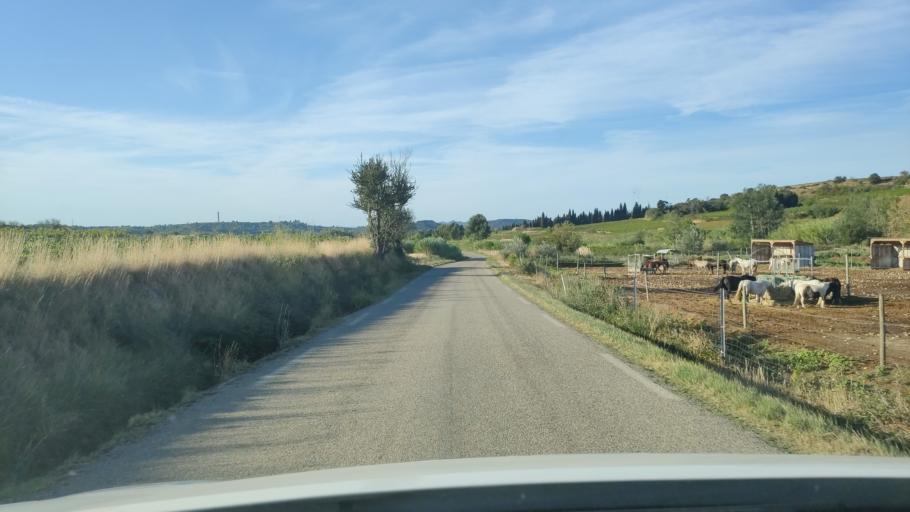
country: FR
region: Languedoc-Roussillon
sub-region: Departement du Gard
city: Saze
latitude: 43.9475
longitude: 4.6546
